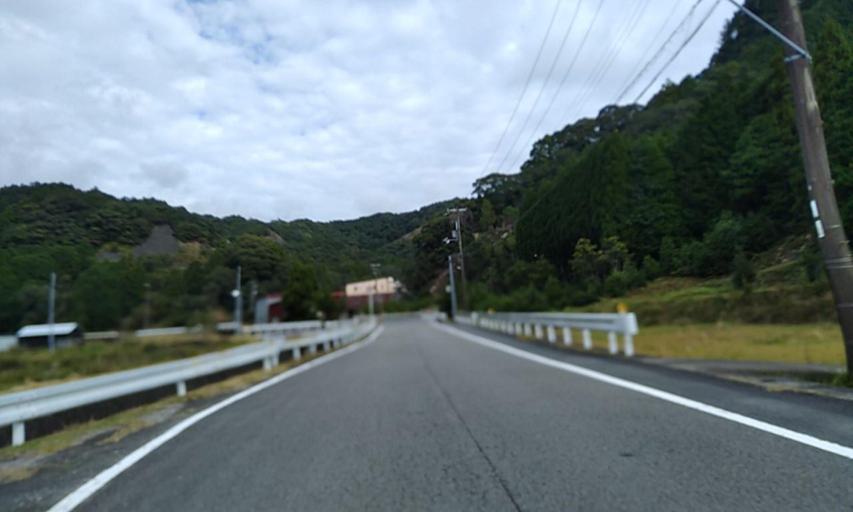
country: JP
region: Wakayama
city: Shingu
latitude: 33.5399
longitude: 135.8292
